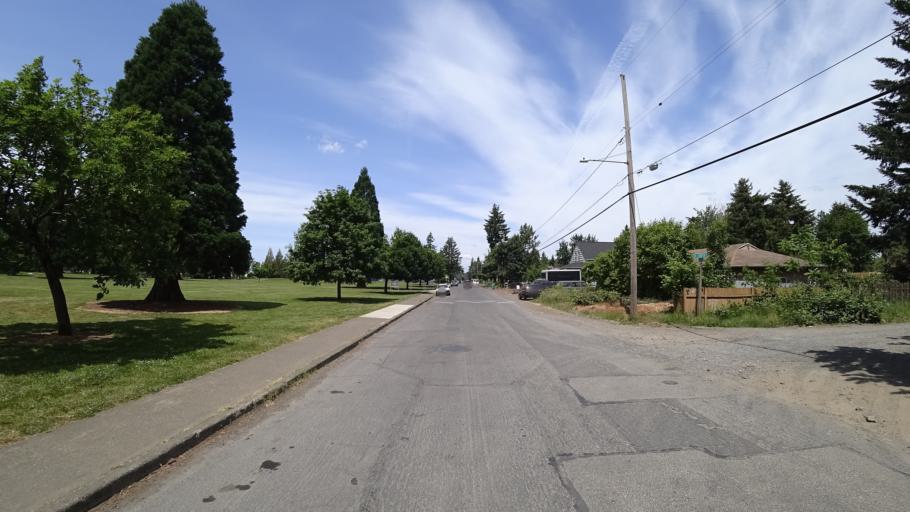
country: US
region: Oregon
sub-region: Multnomah County
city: Lents
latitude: 45.4734
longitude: -122.5997
